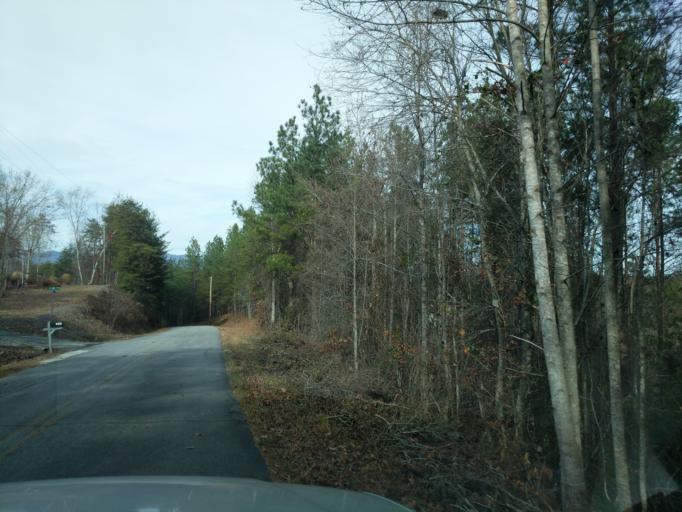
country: US
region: South Carolina
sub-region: Oconee County
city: Walhalla
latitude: 34.8454
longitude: -83.0533
